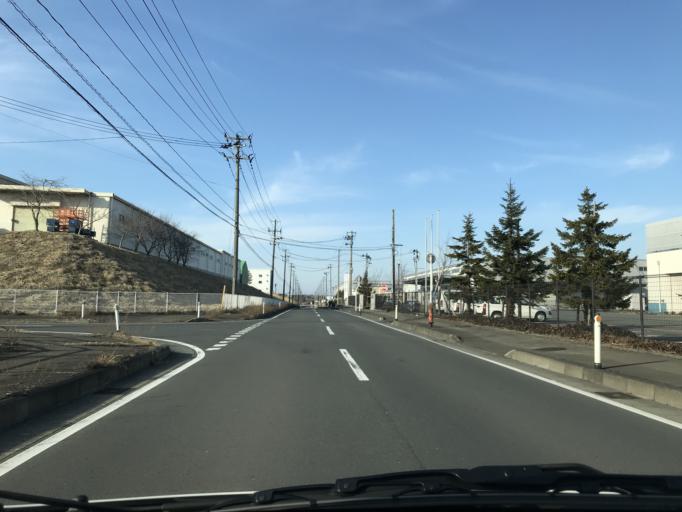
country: JP
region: Iwate
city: Kitakami
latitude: 39.2421
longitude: 141.0928
